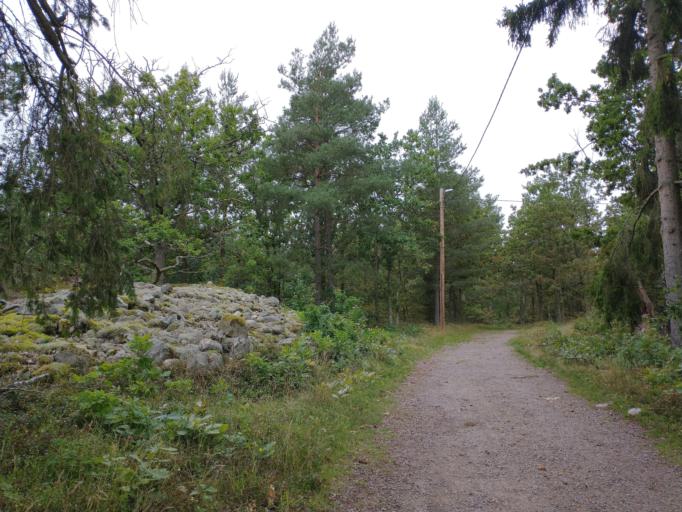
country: SE
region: Kalmar
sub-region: Kalmar Kommun
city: Lindsdal
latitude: 56.7767
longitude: 16.2997
